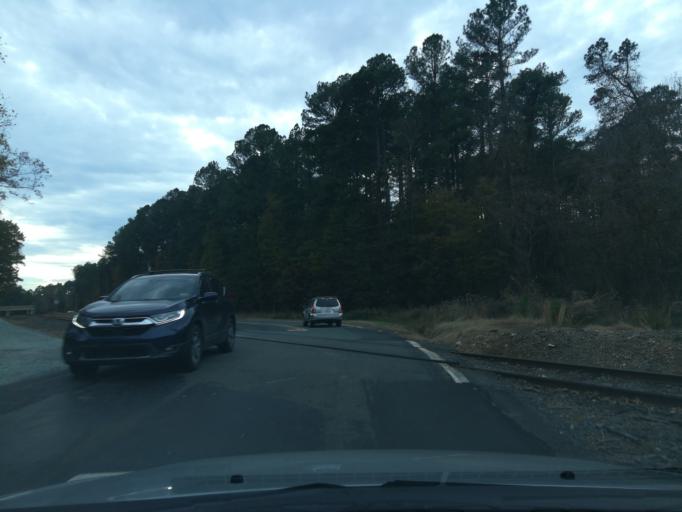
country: US
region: North Carolina
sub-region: Orange County
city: Chapel Hill
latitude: 35.9904
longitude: -79.0730
